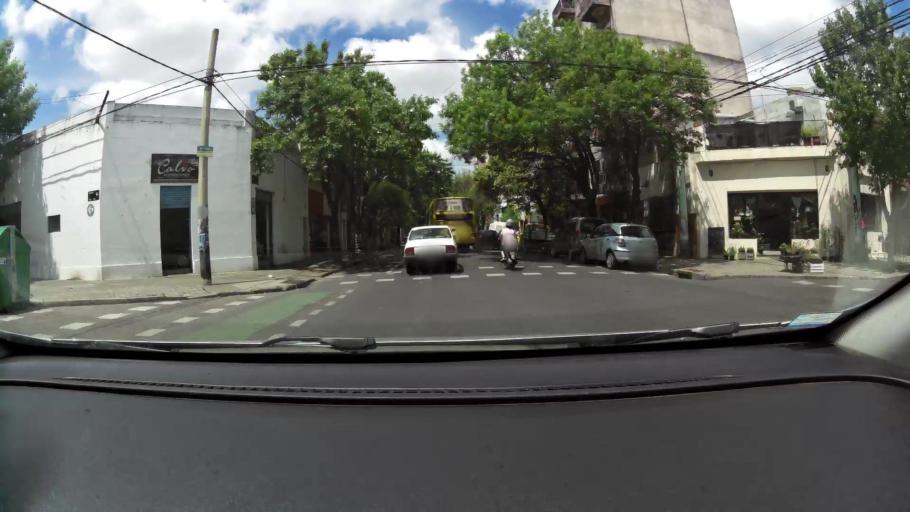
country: AR
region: Santa Fe
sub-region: Departamento de Rosario
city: Rosario
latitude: -32.9682
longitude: -60.6333
